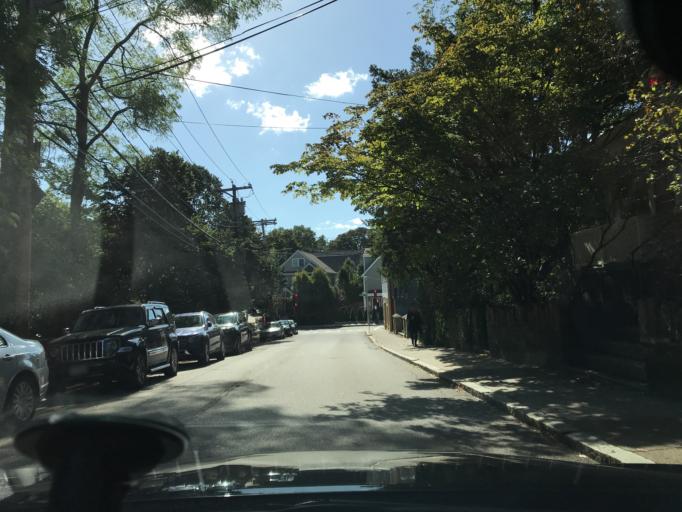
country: US
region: Massachusetts
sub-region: Suffolk County
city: Jamaica Plain
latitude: 42.3118
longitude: -71.1083
